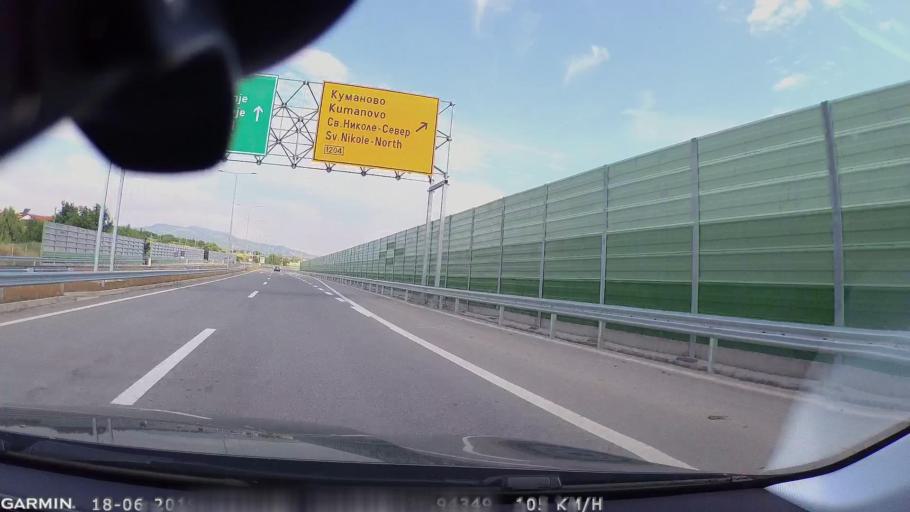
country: MK
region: Sveti Nikole
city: Sveti Nikole
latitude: 41.8749
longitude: 21.9437
